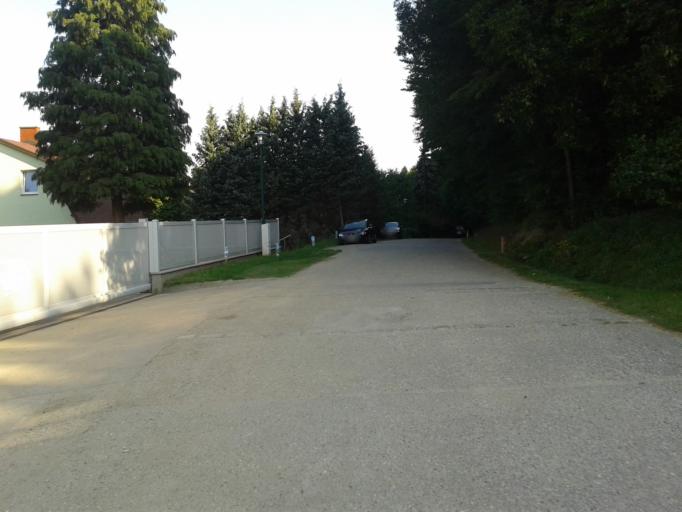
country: AT
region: Lower Austria
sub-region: Politischer Bezirk Wien-Umgebung
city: Gablitz
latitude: 48.2227
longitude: 16.1604
